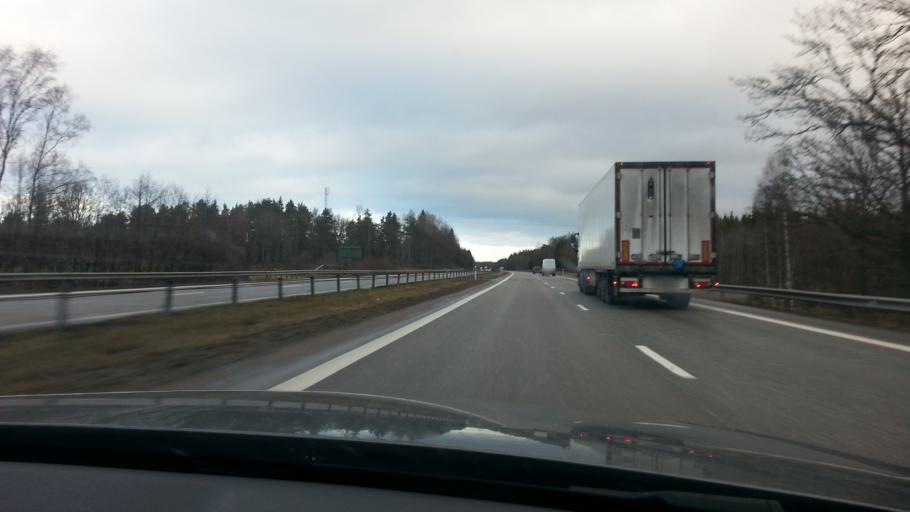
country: SE
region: Joenkoeping
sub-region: Jonkopings Kommun
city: Asa
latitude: 58.0941
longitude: 14.5511
